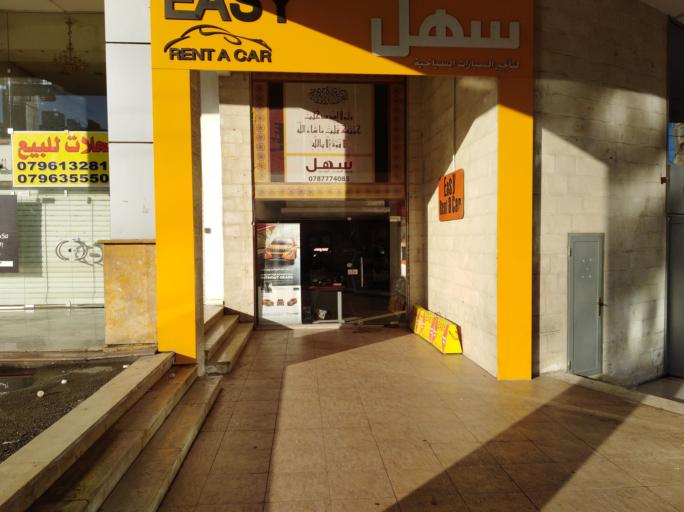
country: JO
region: Amman
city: Wadi as Sir
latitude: 31.9583
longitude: 35.8594
